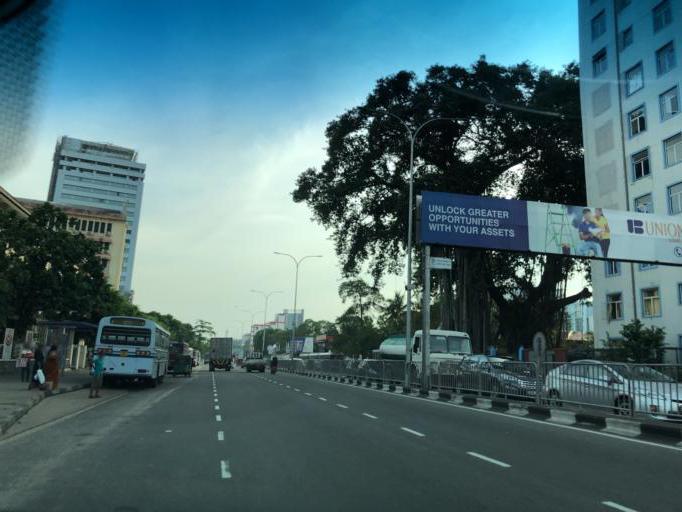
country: LK
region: Western
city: Pita Kotte
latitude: 6.8922
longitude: 79.8770
